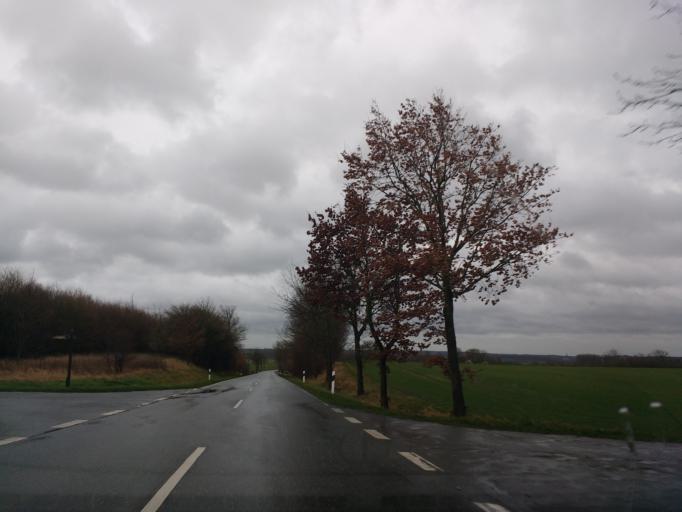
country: DE
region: Schleswig-Holstein
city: Blekendorf
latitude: 54.3171
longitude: 10.6546
